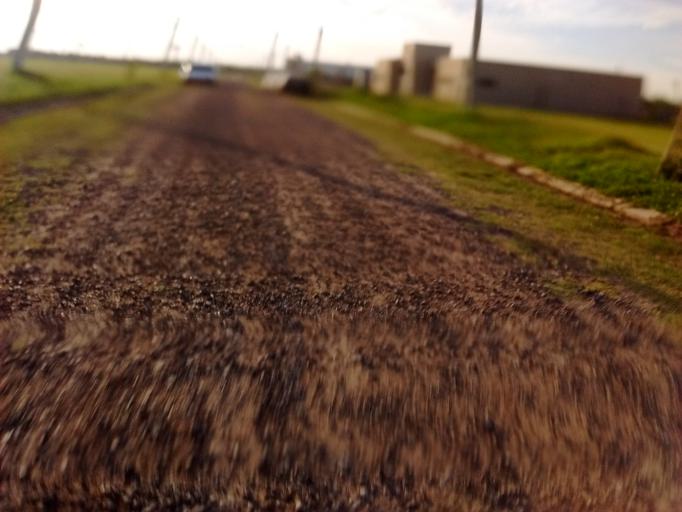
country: AR
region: Santa Fe
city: Roldan
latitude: -32.9283
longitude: -60.8733
